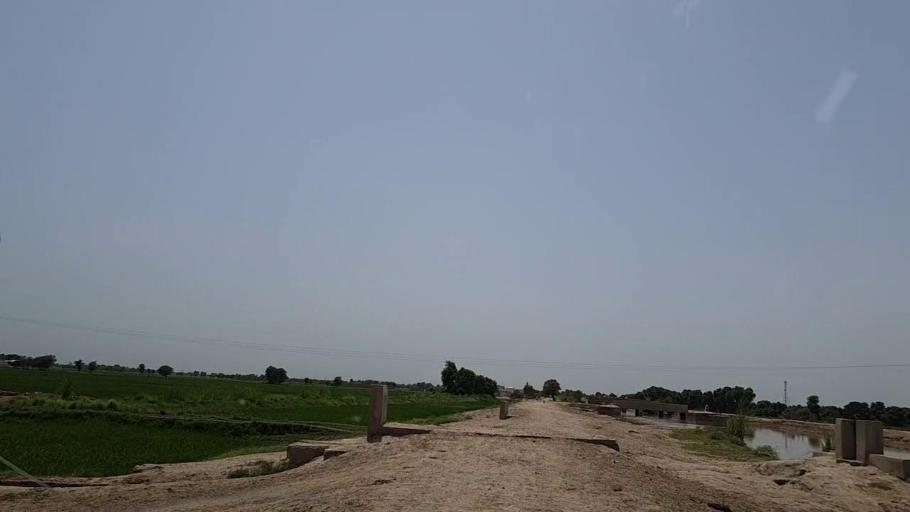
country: PK
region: Sindh
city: Tharu Shah
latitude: 26.9881
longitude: 68.0880
